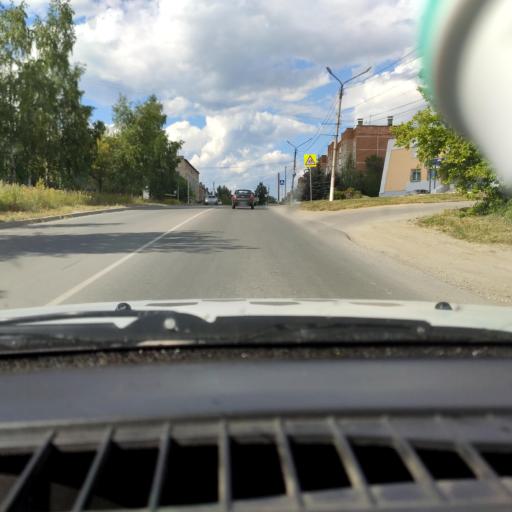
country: RU
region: Chelyabinsk
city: Miass
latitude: 55.0776
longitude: 60.0932
